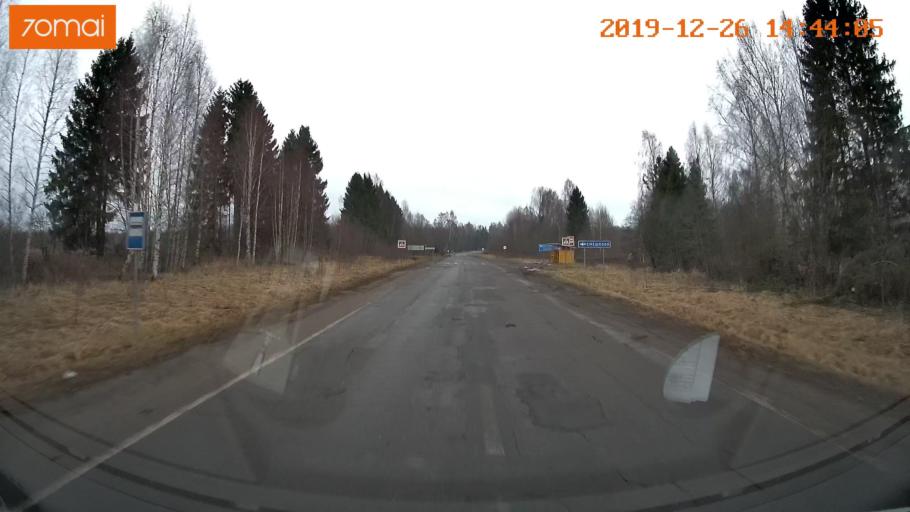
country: RU
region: Jaroslavl
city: Poshekhon'ye
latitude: 58.3511
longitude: 39.0472
